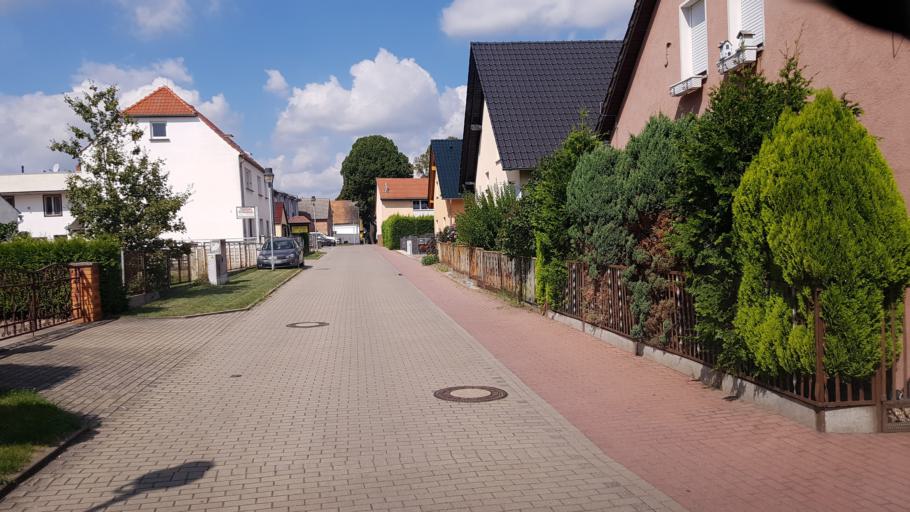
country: DE
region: Brandenburg
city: Lubbenau
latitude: 51.8611
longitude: 13.9324
